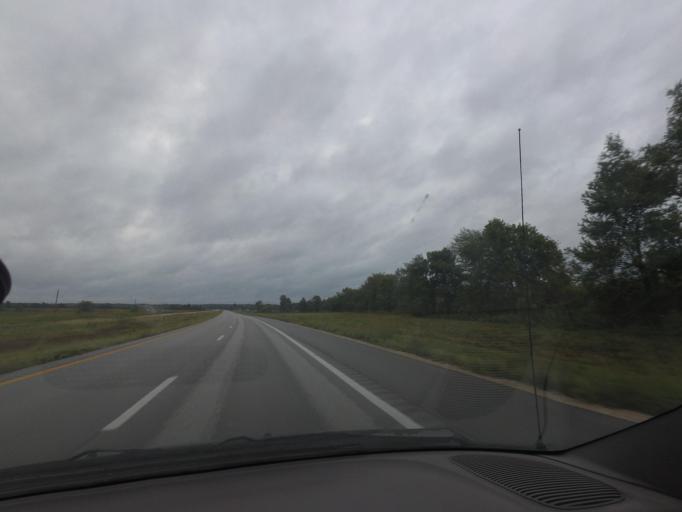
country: US
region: Missouri
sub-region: Shelby County
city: Shelbina
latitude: 39.6667
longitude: -91.9246
